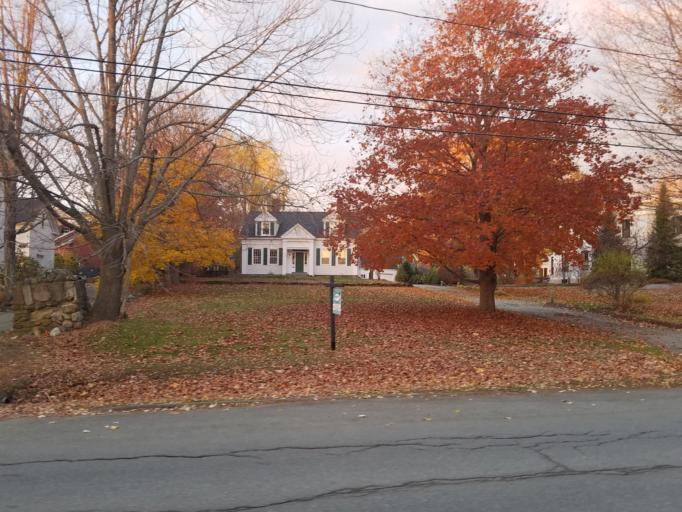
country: US
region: Maine
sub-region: Waldo County
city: Belfast
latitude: 44.4221
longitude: -69.0008
